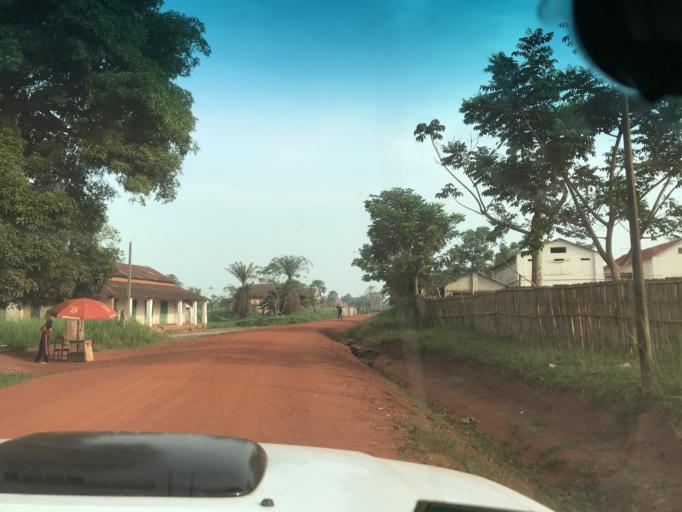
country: CD
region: Eastern Province
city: Buta
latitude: 2.7912
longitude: 24.7265
